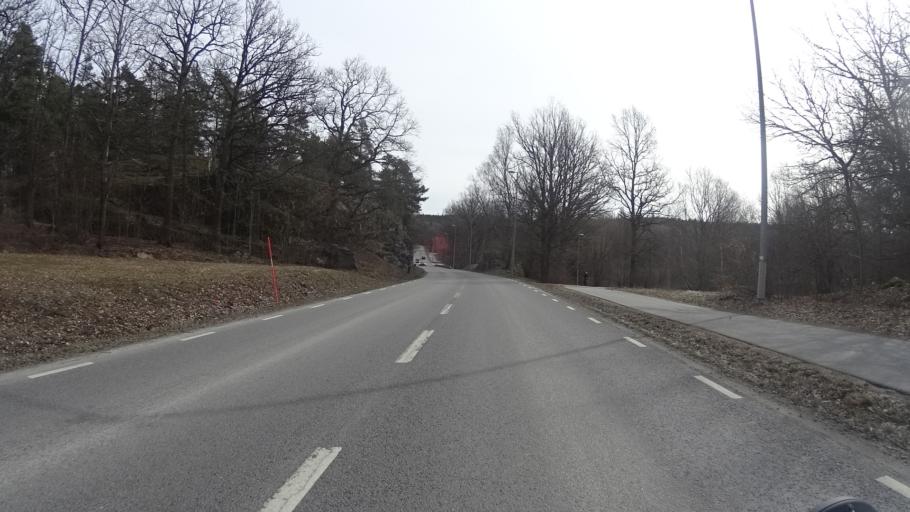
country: SE
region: Stockholm
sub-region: Nacka Kommun
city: Nacka
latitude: 59.2917
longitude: 18.1513
